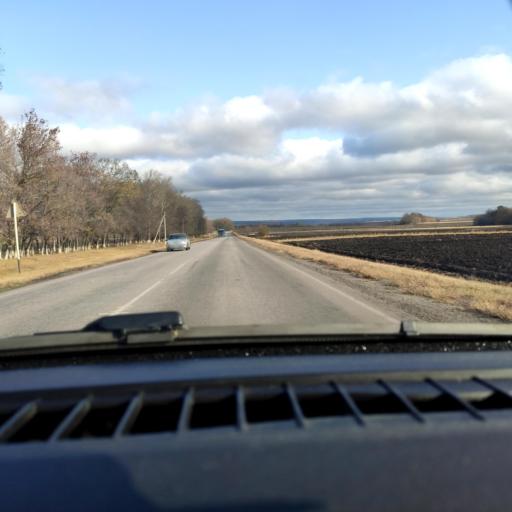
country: RU
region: Belgorod
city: Ilovka
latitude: 50.7345
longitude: 38.7012
